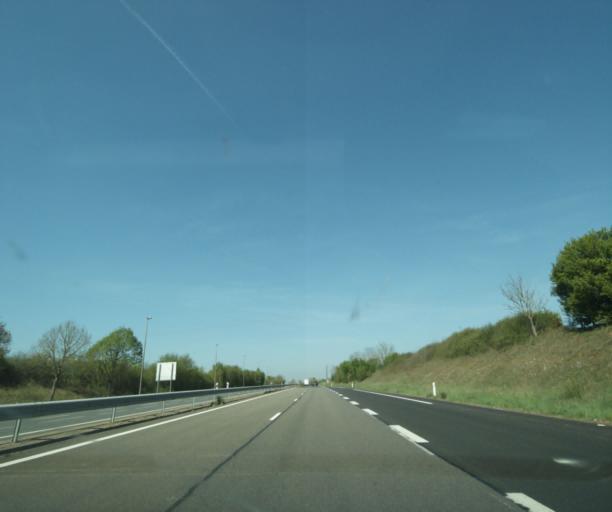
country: FR
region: Bourgogne
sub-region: Departement de la Nievre
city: La Charite-sur-Loire
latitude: 47.1882
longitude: 3.0342
